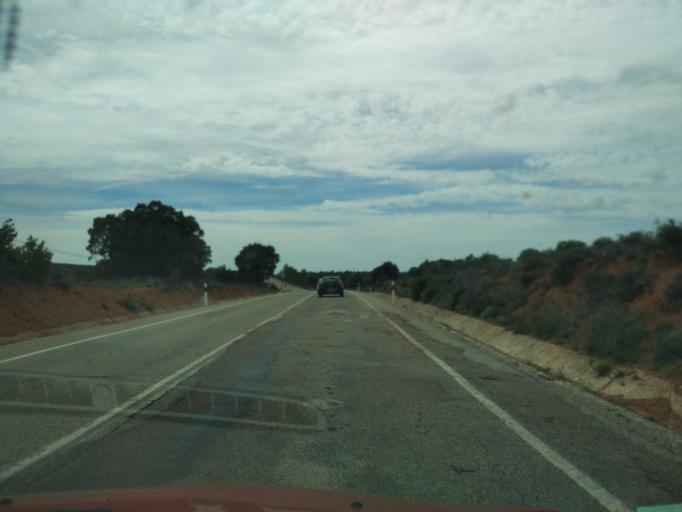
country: ES
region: Castille-La Mancha
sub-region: Provincia de Guadalajara
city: Algora
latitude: 41.0063
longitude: -2.6884
